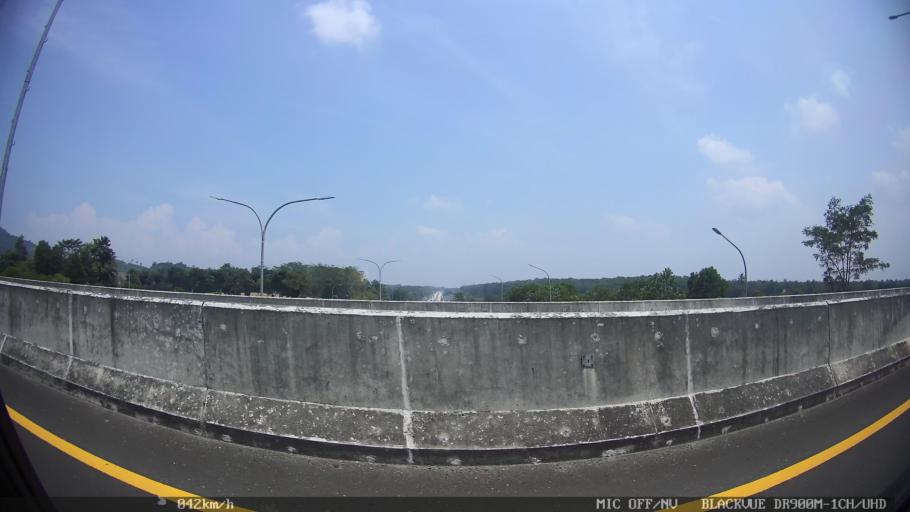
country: ID
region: Lampung
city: Panjang
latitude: -5.3953
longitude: 105.3496
